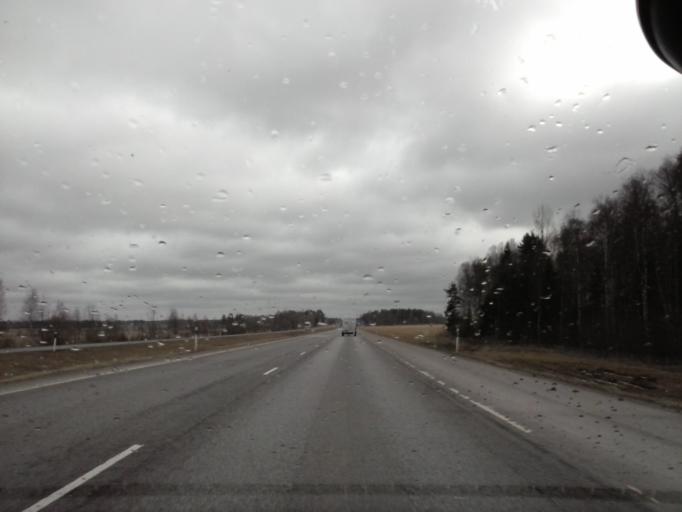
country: EE
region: Harju
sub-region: Rae vald
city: Vaida
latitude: 59.2673
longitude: 24.9948
